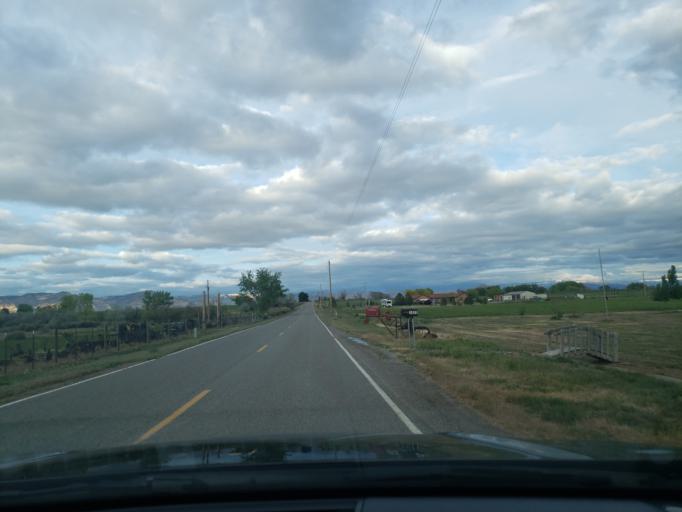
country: US
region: Colorado
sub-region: Mesa County
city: Fruita
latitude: 39.2221
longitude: -108.7156
